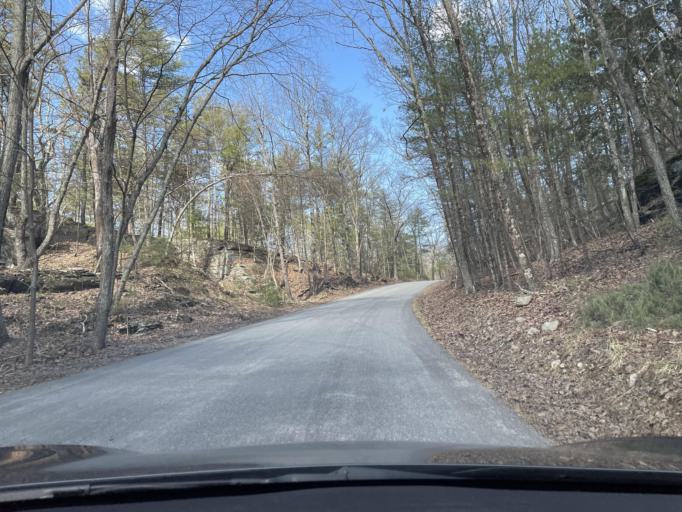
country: US
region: New York
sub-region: Ulster County
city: West Hurley
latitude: 41.9622
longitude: -74.1113
